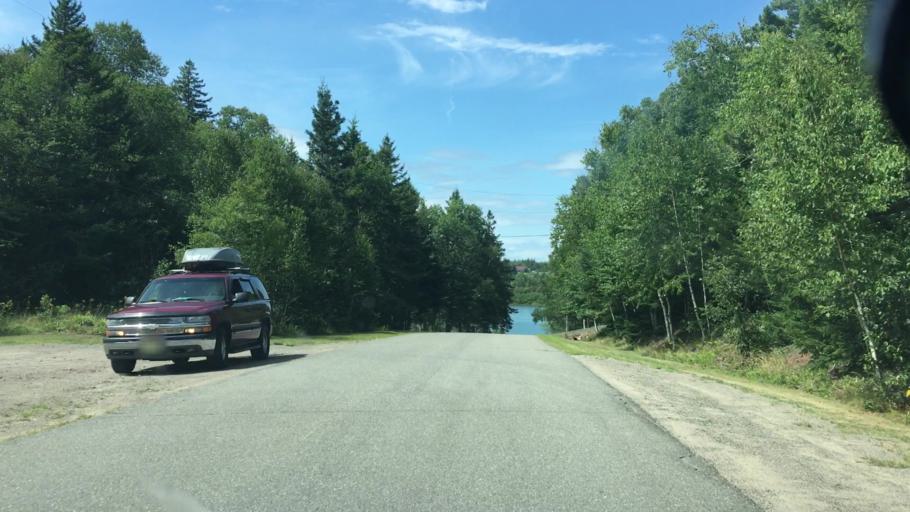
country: US
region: Maine
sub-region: Washington County
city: Eastport
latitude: 44.9338
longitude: -67.0455
